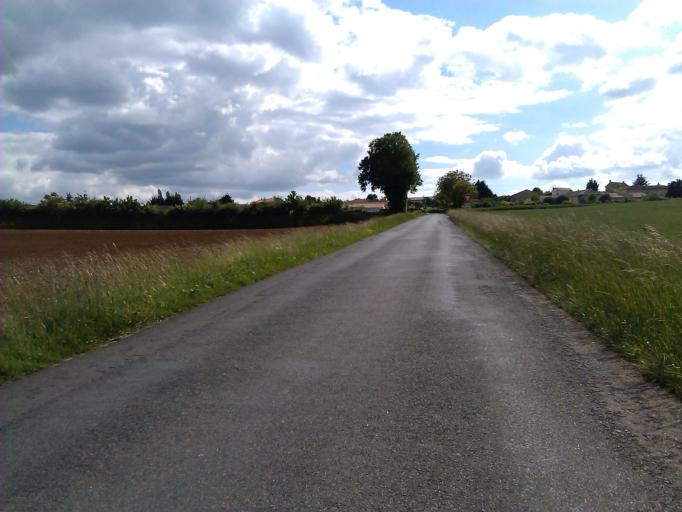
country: FR
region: Poitou-Charentes
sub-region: Departement de la Charente
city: Mansle
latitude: 45.8966
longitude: 0.2068
